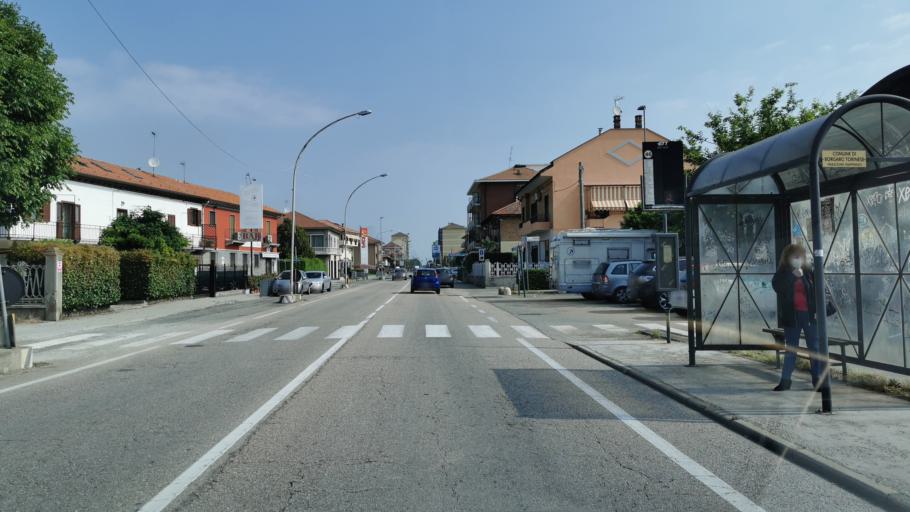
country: IT
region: Piedmont
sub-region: Provincia di Torino
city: Leini
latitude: 45.1440
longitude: 7.7067
